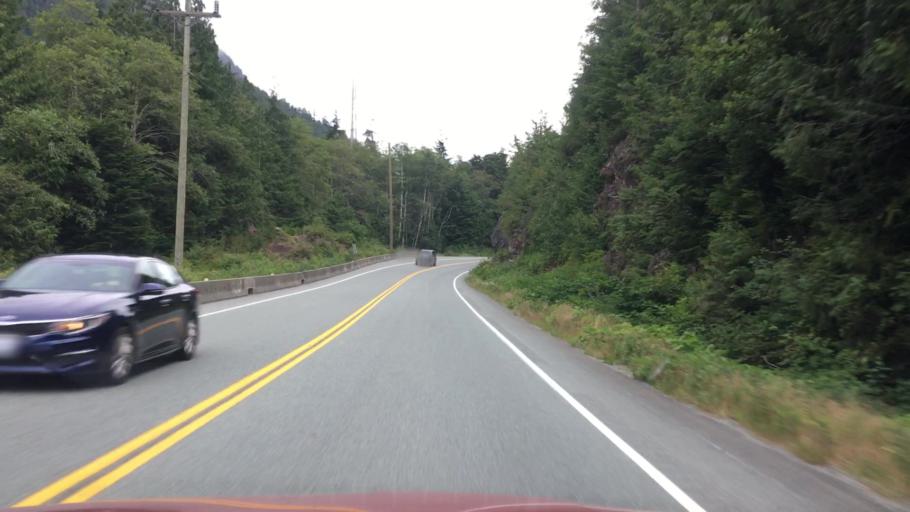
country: CA
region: British Columbia
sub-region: Regional District of Alberni-Clayoquot
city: Ucluelet
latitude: 49.2022
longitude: -125.3780
